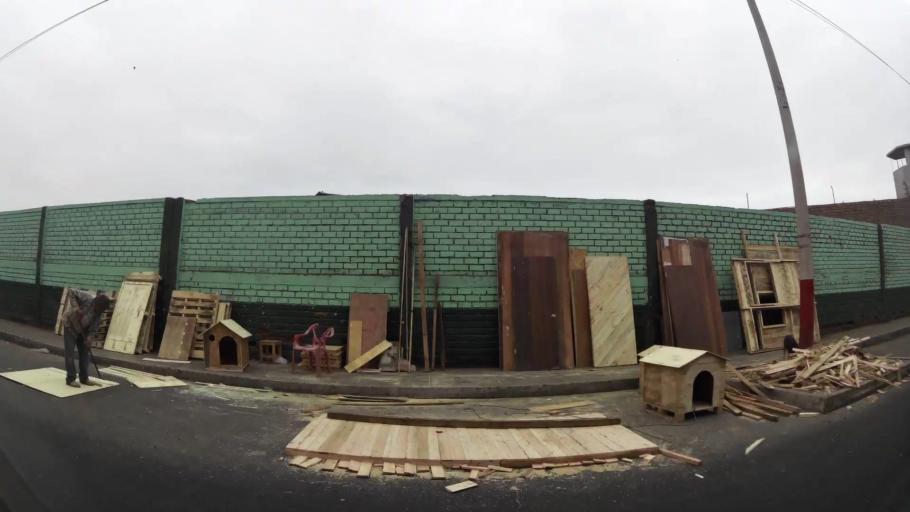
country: PE
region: Callao
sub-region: Callao
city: Callao
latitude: -12.0518
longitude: -77.1405
